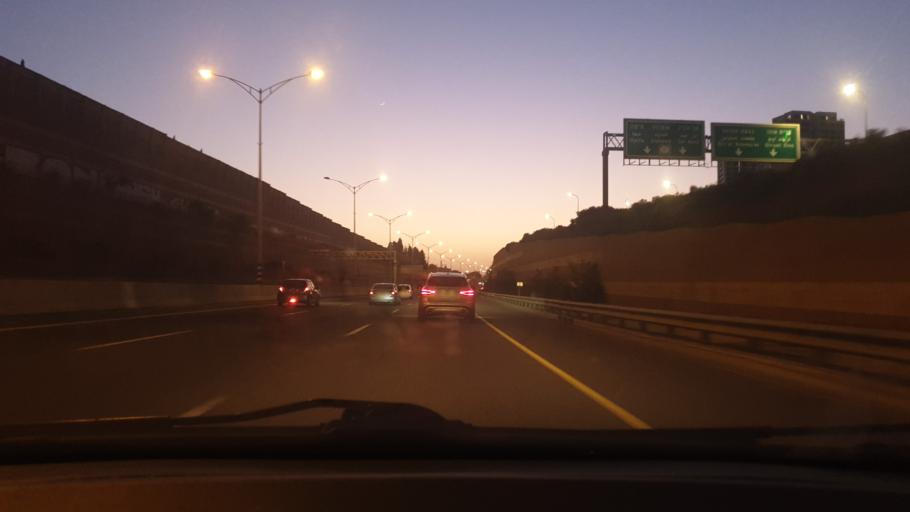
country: IL
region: Tel Aviv
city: Giv`at Shemu'el
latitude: 32.0689
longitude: 34.8590
